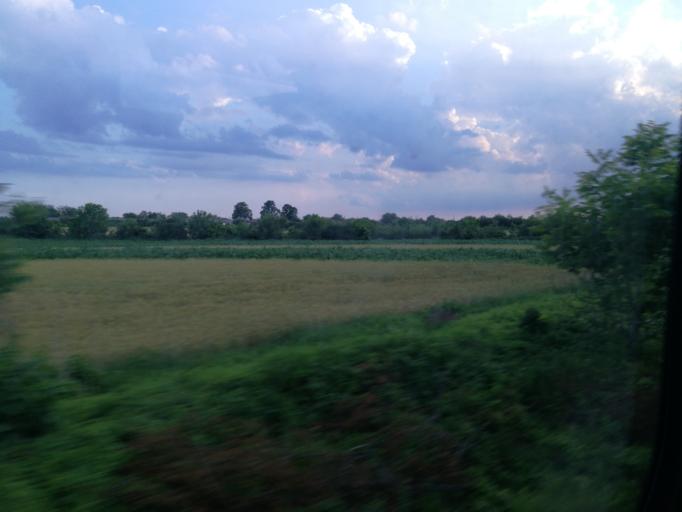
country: RO
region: Dambovita
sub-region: Comuna Titu
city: Titu
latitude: 44.6667
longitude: 25.5366
